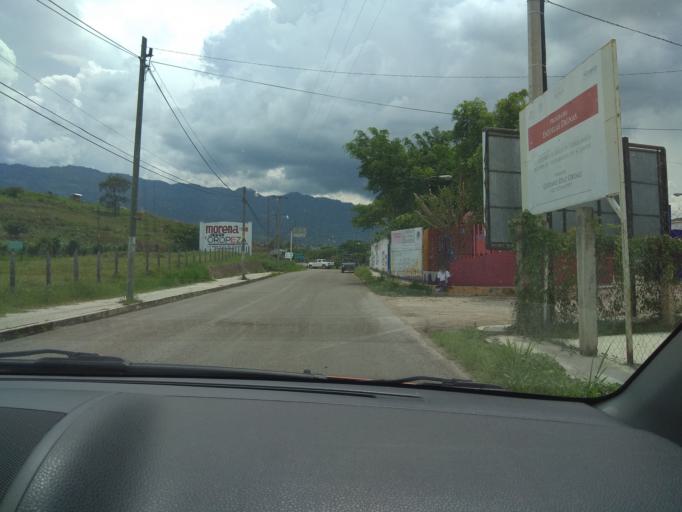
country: MX
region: Chiapas
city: Ocosingo
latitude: 16.8960
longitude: -92.0723
